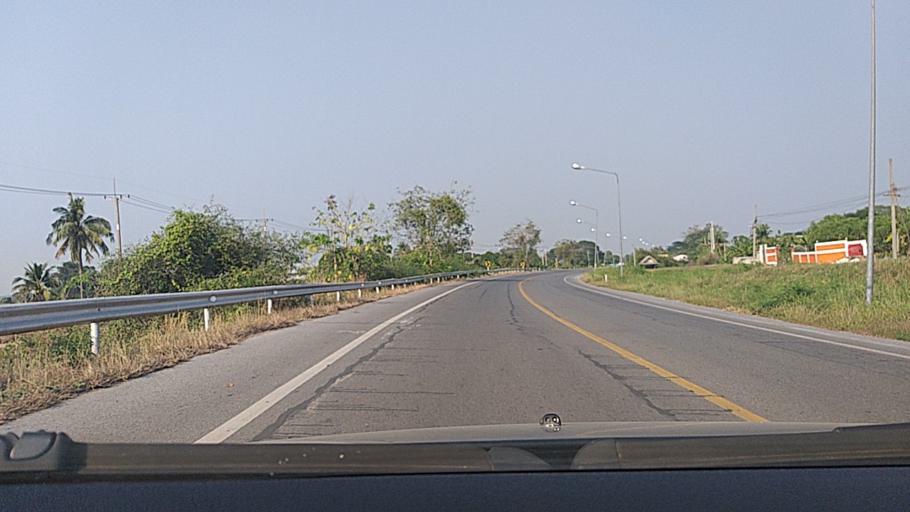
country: TH
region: Sing Buri
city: Tha Chang
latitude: 14.7306
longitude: 100.4307
